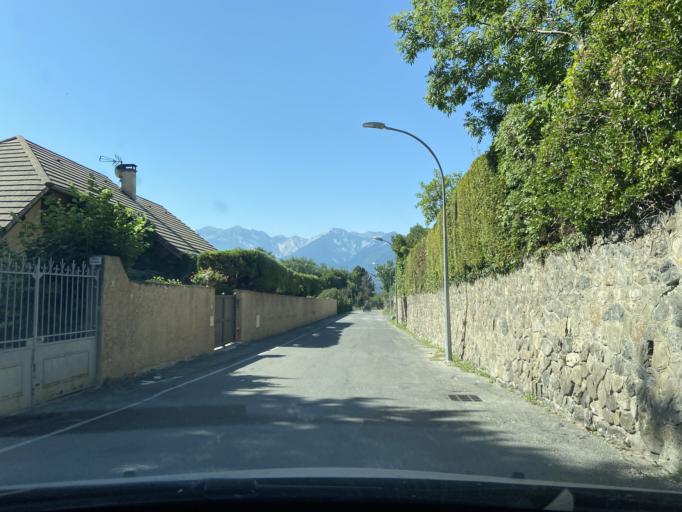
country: FR
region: Provence-Alpes-Cote d'Azur
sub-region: Departement des Hautes-Alpes
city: Embrun
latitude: 44.5648
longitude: 6.4921
